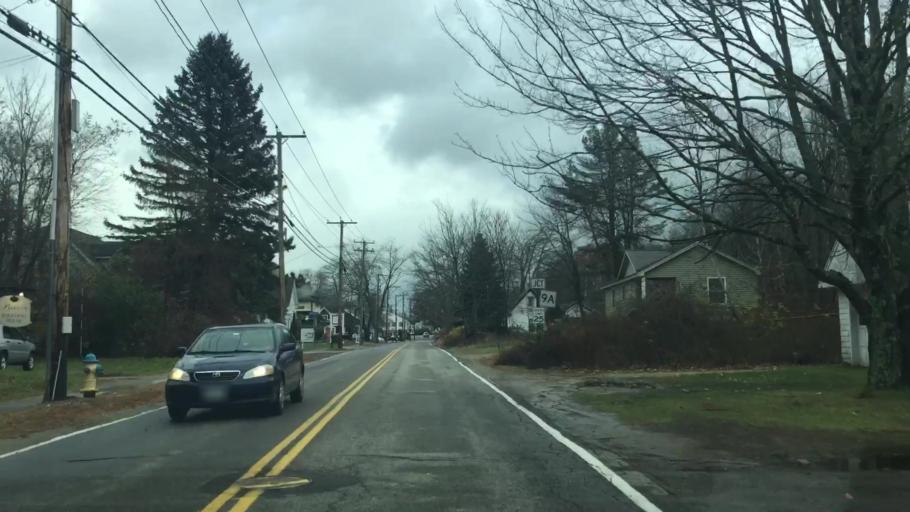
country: US
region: Maine
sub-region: York County
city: Kennebunkport
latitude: 43.3591
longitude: -70.4858
